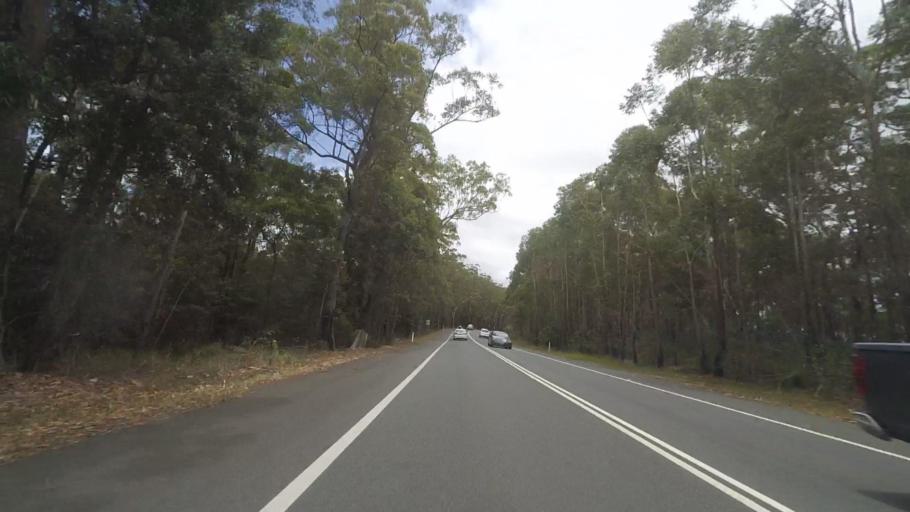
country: AU
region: New South Wales
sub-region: Shoalhaven Shire
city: Milton
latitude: -35.1490
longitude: 150.4595
